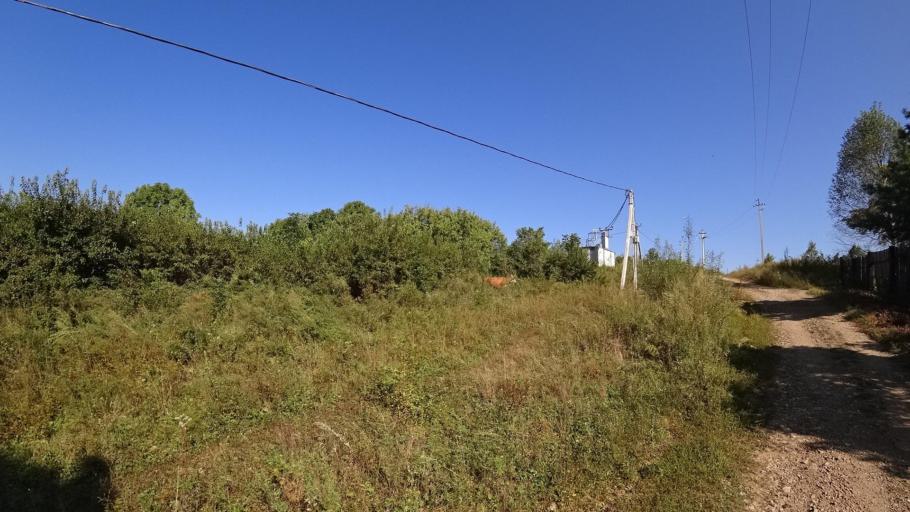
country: RU
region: Jewish Autonomous Oblast
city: Bira
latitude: 49.0089
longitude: 132.4689
